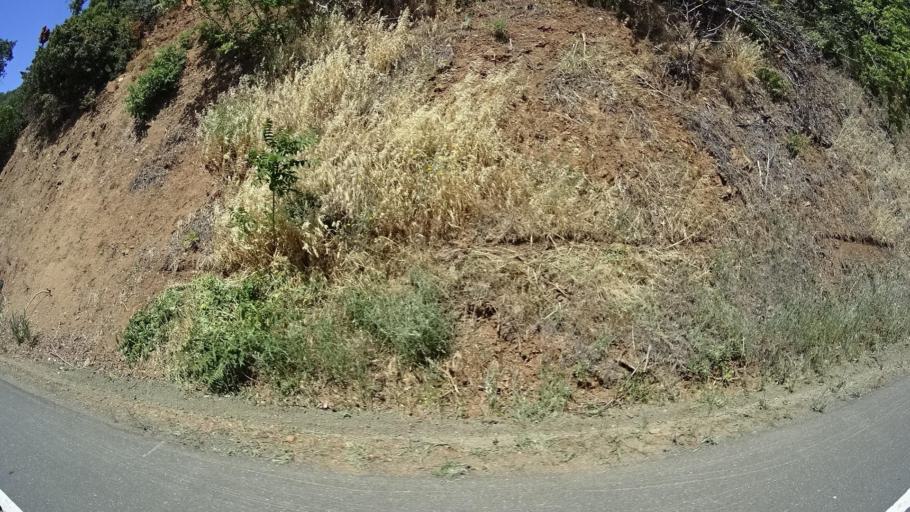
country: US
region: California
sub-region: Lake County
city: Clearlake Oaks
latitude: 39.0201
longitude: -122.6953
